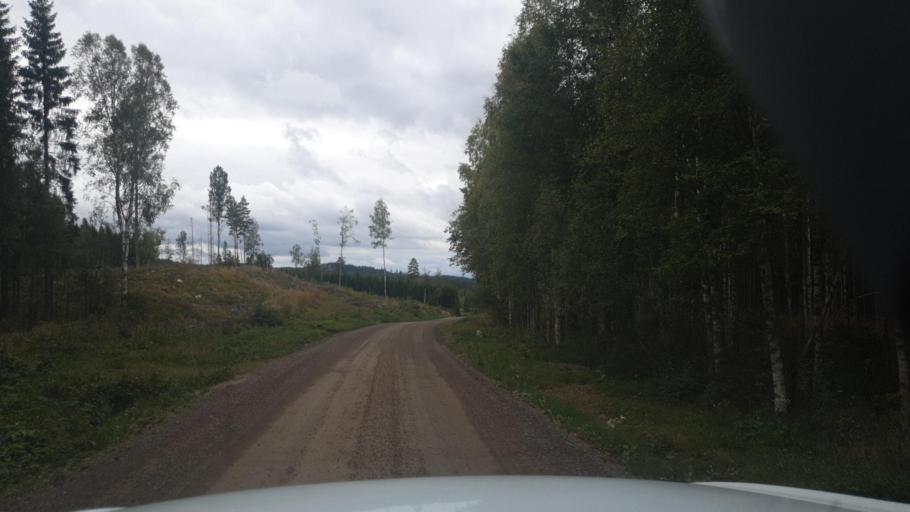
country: SE
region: Vaermland
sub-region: Arvika Kommun
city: Arvika
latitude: 59.9449
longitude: 12.6614
